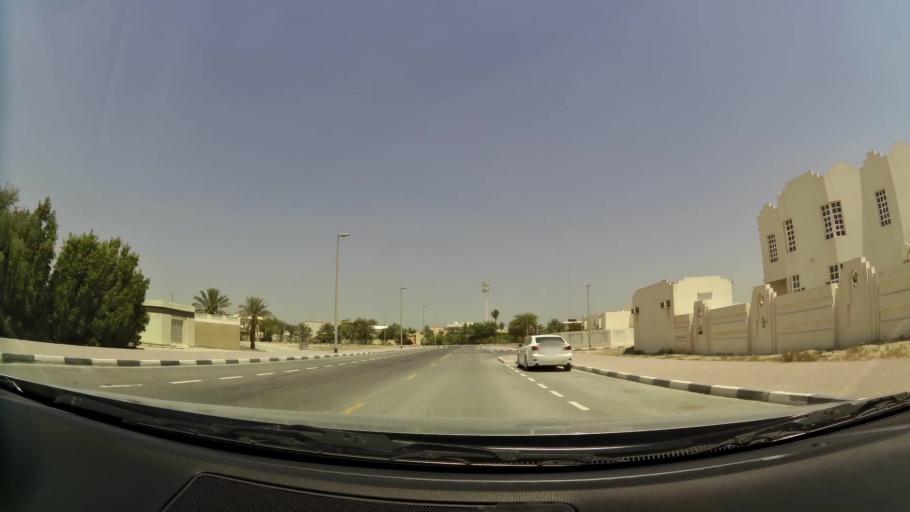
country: AE
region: Dubai
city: Dubai
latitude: 25.1979
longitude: 55.2586
